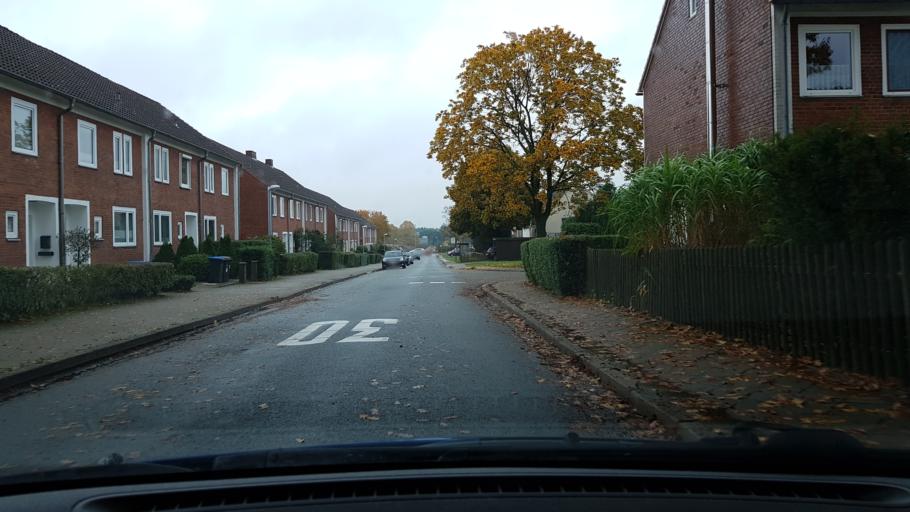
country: DE
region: Lower Saxony
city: Lueneburg
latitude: 53.2490
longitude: 10.4412
